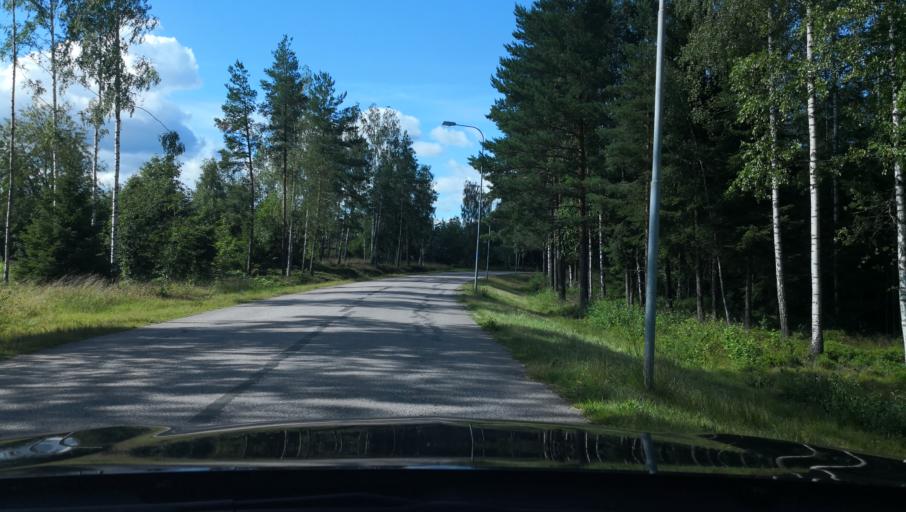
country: SE
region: Vaestmanland
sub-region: Surahammars Kommun
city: Surahammar
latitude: 59.6956
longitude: 16.2428
